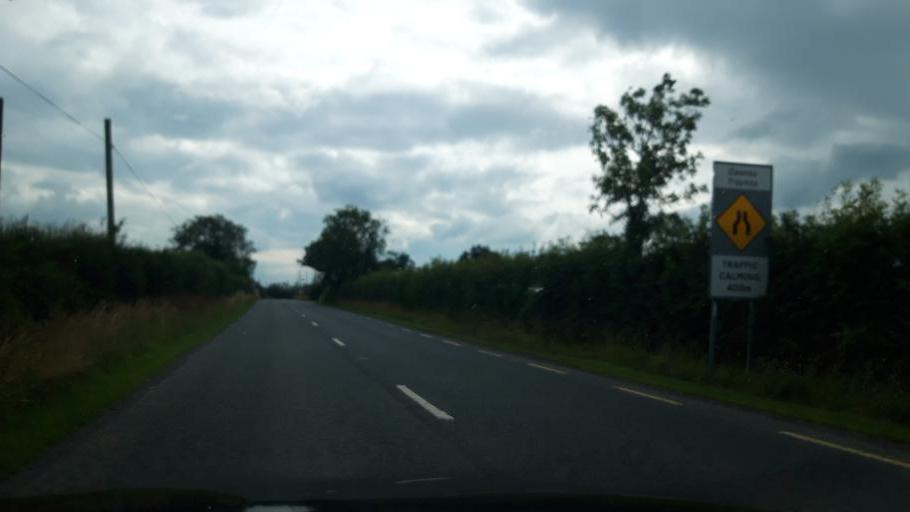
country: IE
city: Ballylinan
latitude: 52.8673
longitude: -7.1013
